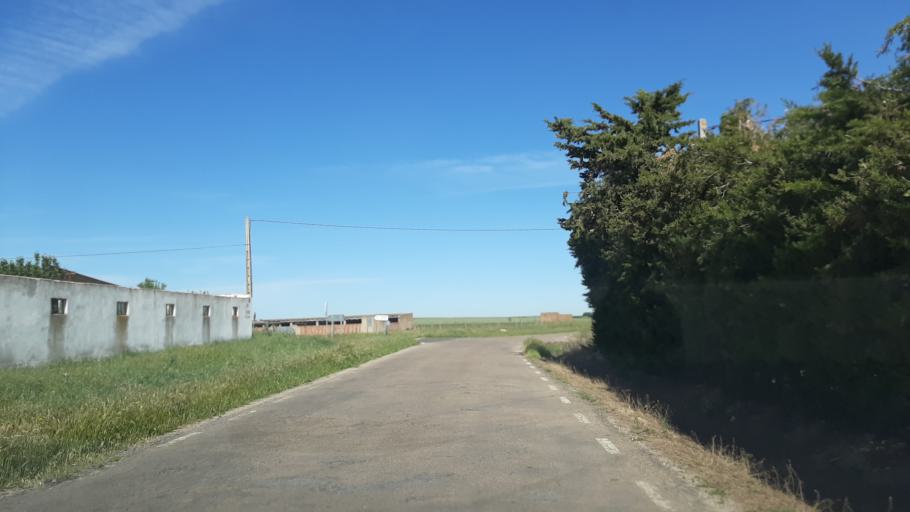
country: ES
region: Castille and Leon
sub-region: Provincia de Salamanca
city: Pedrosillo de Alba
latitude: 40.8205
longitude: -5.3956
